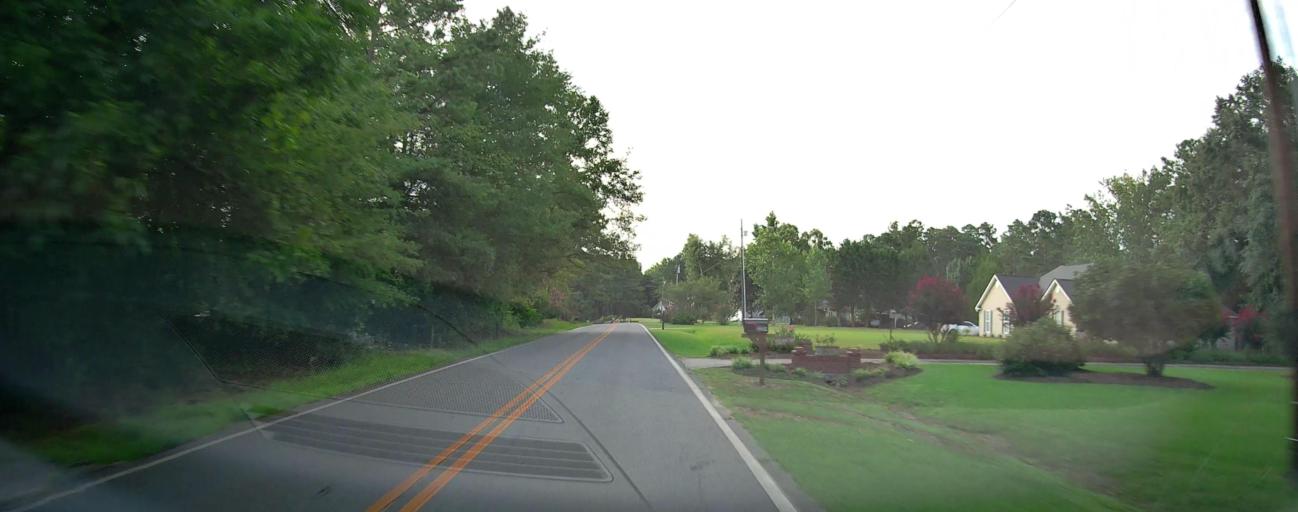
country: US
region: Georgia
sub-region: Peach County
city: Byron
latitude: 32.7215
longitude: -83.7562
